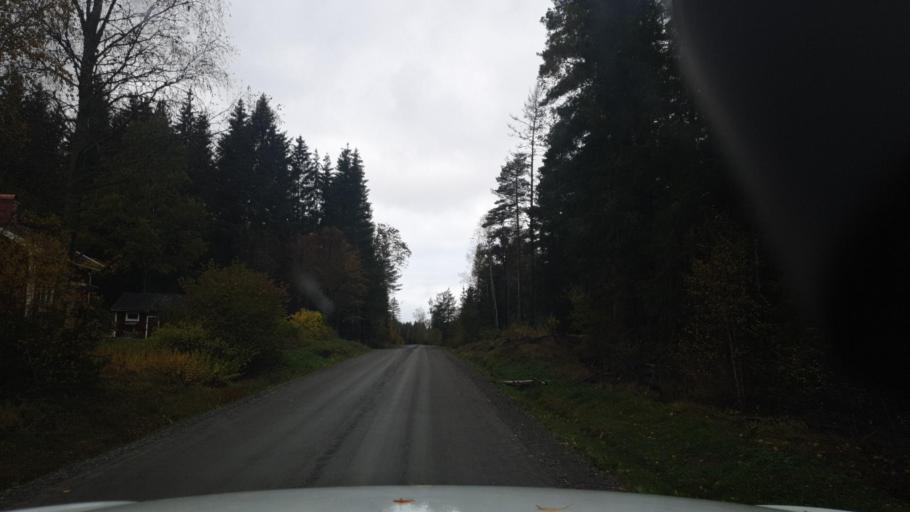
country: SE
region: Vaermland
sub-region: Karlstads Kommun
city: Edsvalla
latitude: 59.4509
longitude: 13.1329
